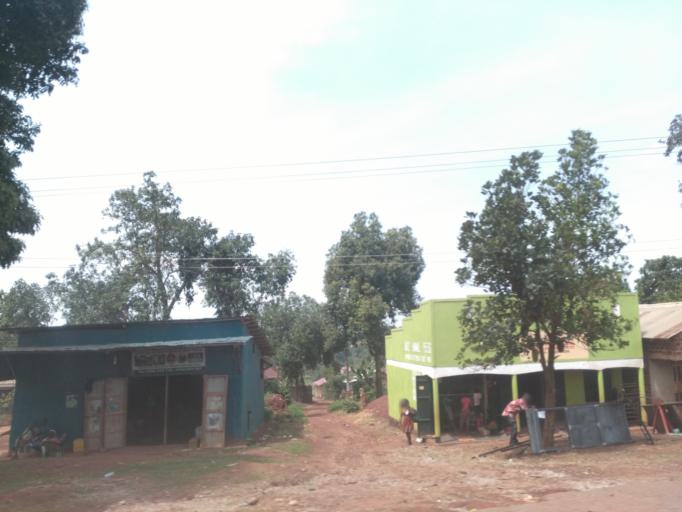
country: UG
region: Central Region
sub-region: Wakiso District
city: Kireka
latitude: 0.4589
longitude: 32.6057
